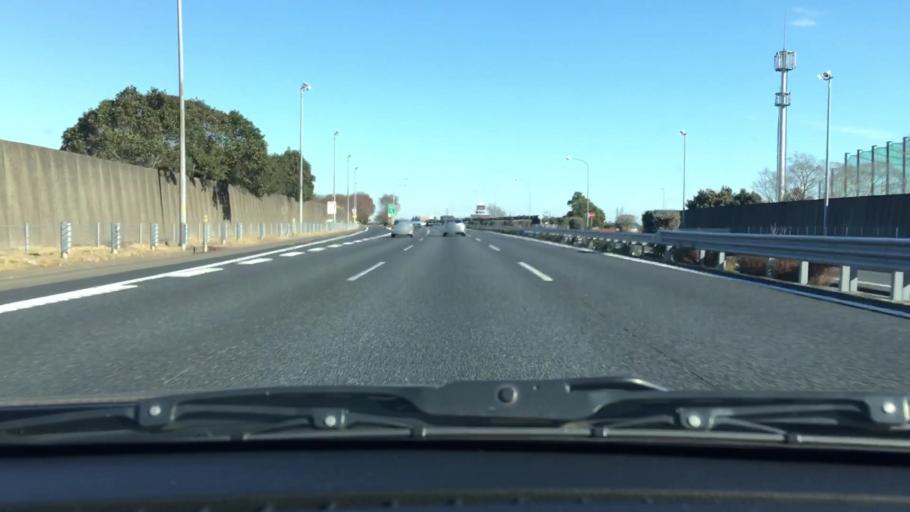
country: JP
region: Chiba
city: Narita
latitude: 35.7417
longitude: 140.3087
